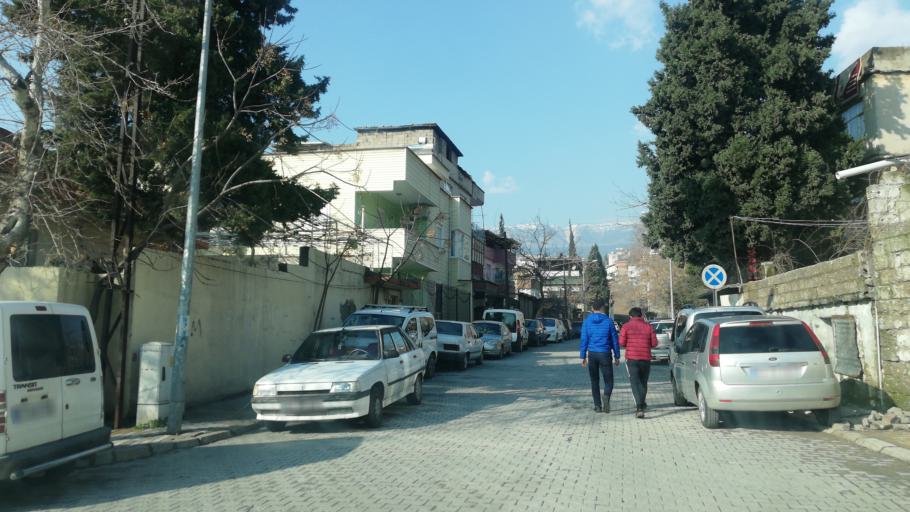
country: TR
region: Kahramanmaras
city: Kahramanmaras
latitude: 37.5792
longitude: 36.9335
